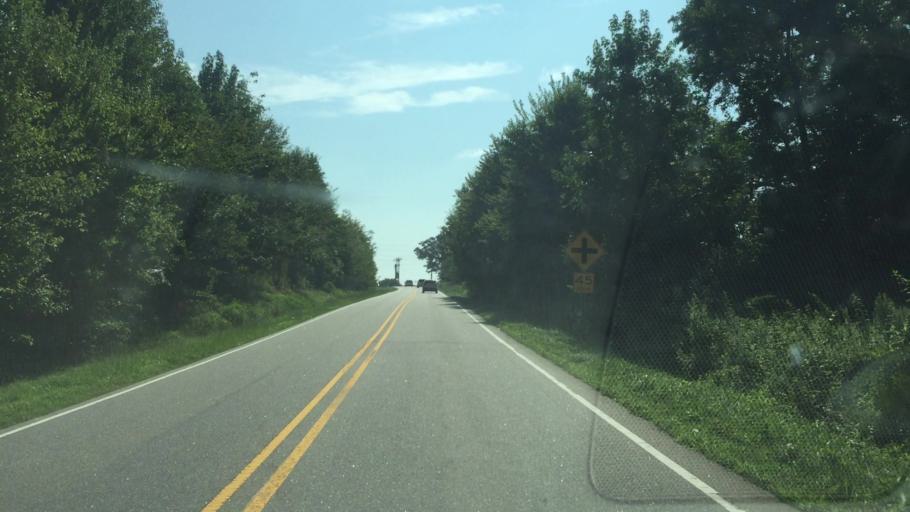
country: US
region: North Carolina
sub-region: Union County
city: Unionville
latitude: 35.1304
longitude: -80.4822
